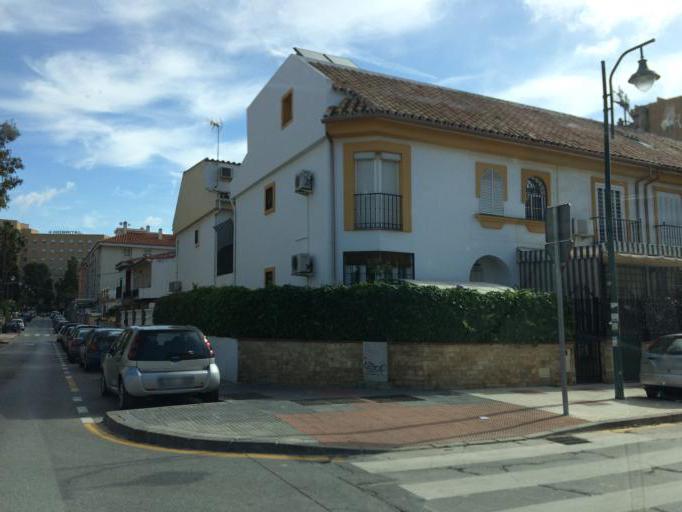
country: ES
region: Andalusia
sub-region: Provincia de Malaga
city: Malaga
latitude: 36.7208
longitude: -4.4506
